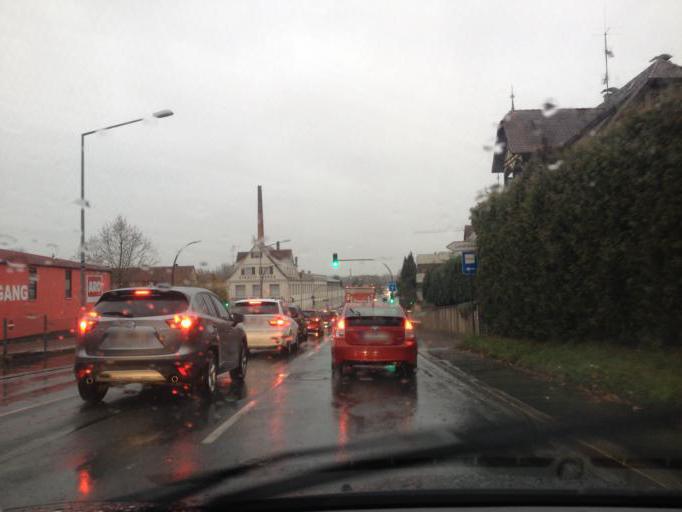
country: DE
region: Bavaria
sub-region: Regierungsbezirk Mittelfranken
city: Lauf an der Pegnitz
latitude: 49.5080
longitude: 11.2715
